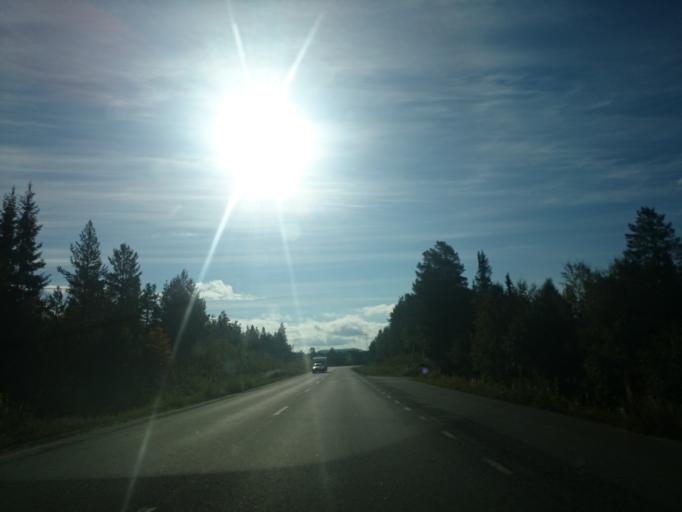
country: NO
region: Hedmark
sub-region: Engerdal
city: Engerdal
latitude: 62.5244
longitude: 12.5854
